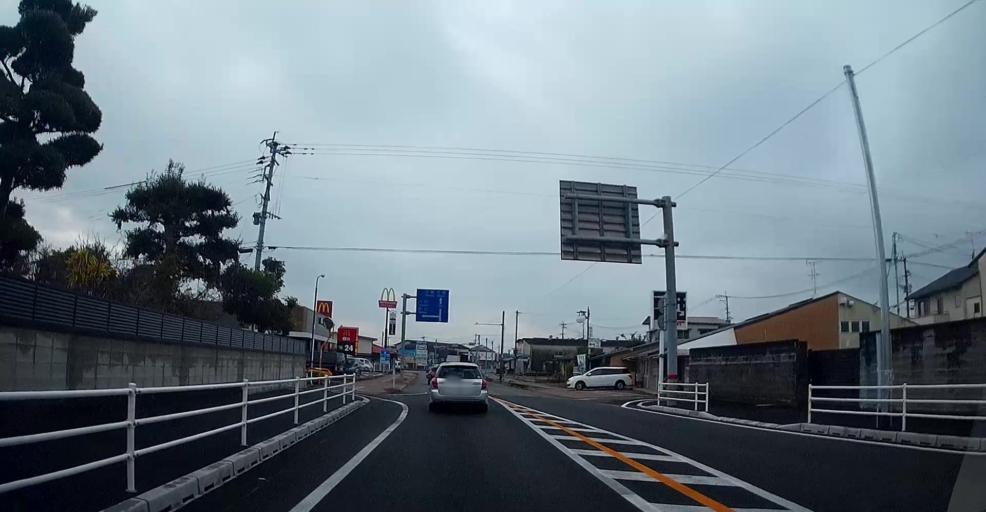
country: JP
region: Kumamoto
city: Matsubase
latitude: 32.6507
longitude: 130.6745
